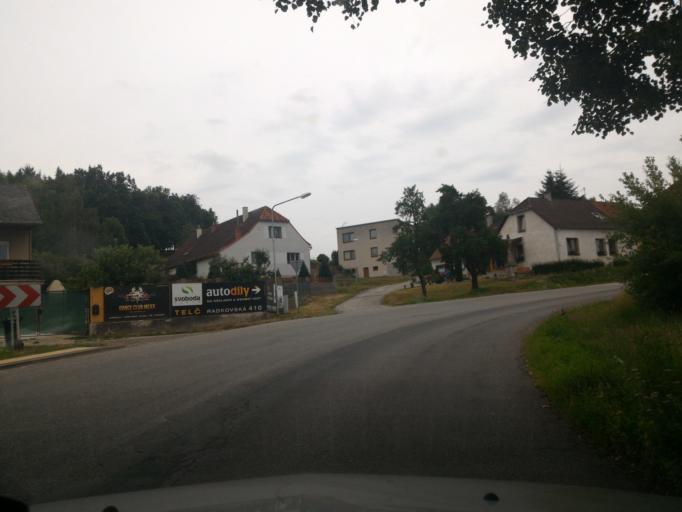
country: CZ
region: Vysocina
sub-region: Okres Jihlava
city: Telc
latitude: 49.1853
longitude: 15.4173
